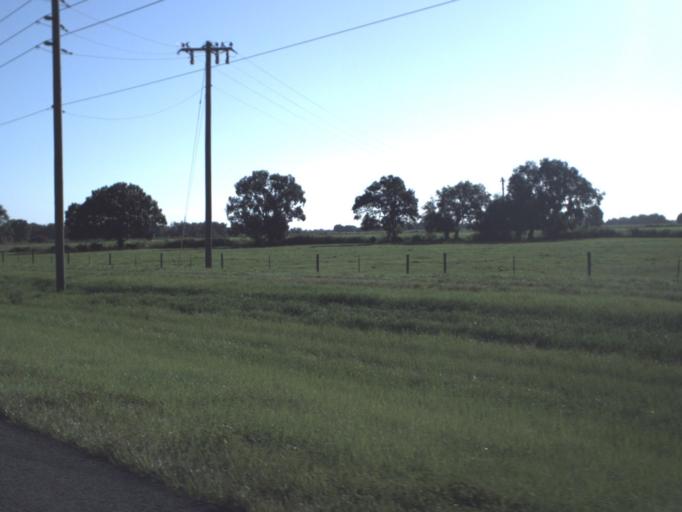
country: US
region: Florida
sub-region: DeSoto County
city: Nocatee
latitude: 27.1025
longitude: -81.9354
